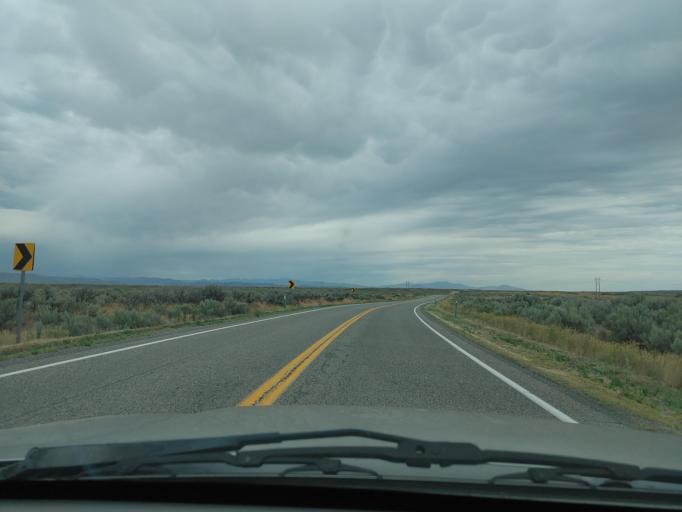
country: US
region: Idaho
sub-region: Lincoln County
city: Shoshone
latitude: 43.0826
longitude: -114.0998
